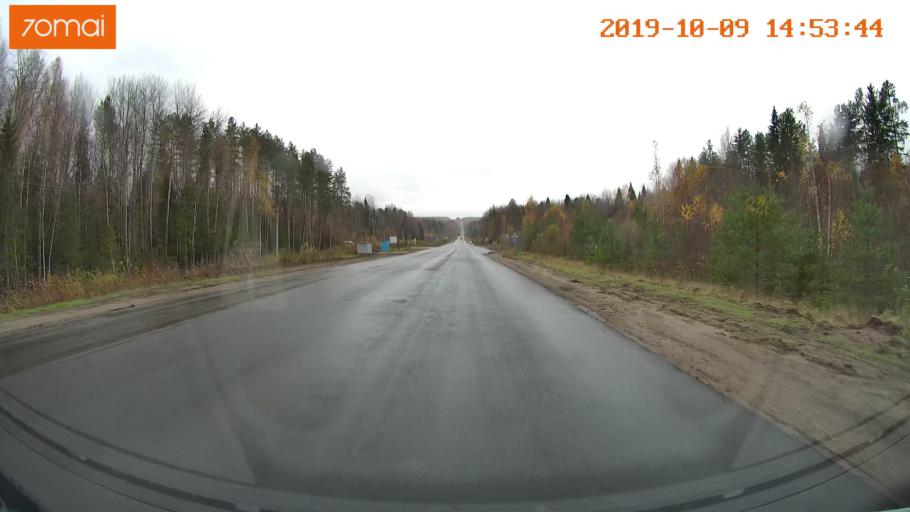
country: RU
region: Kostroma
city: Chistyye Bory
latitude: 58.3641
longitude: 41.6398
